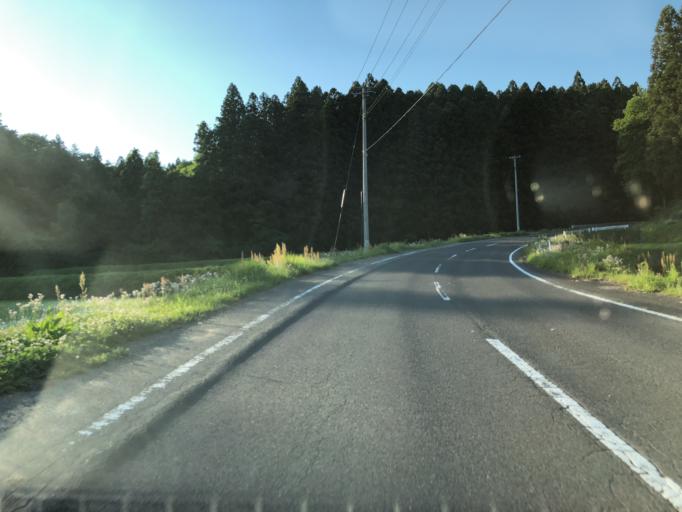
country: JP
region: Fukushima
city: Ishikawa
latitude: 37.0025
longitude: 140.4336
